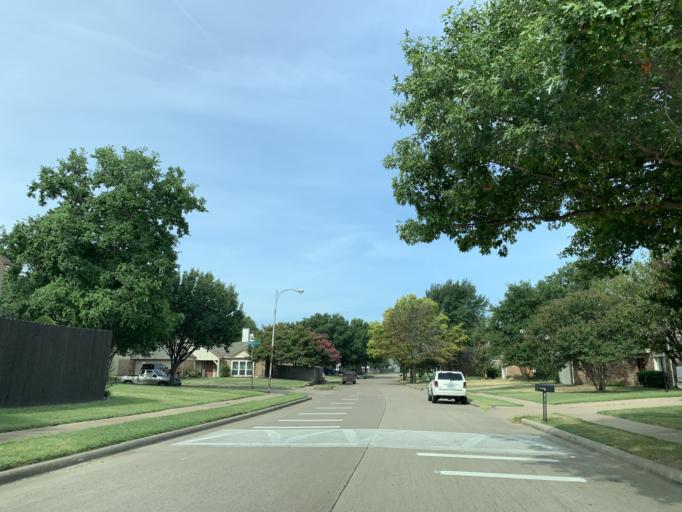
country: US
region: Texas
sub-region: Dallas County
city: Grand Prairie
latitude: 32.6645
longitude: -97.0047
